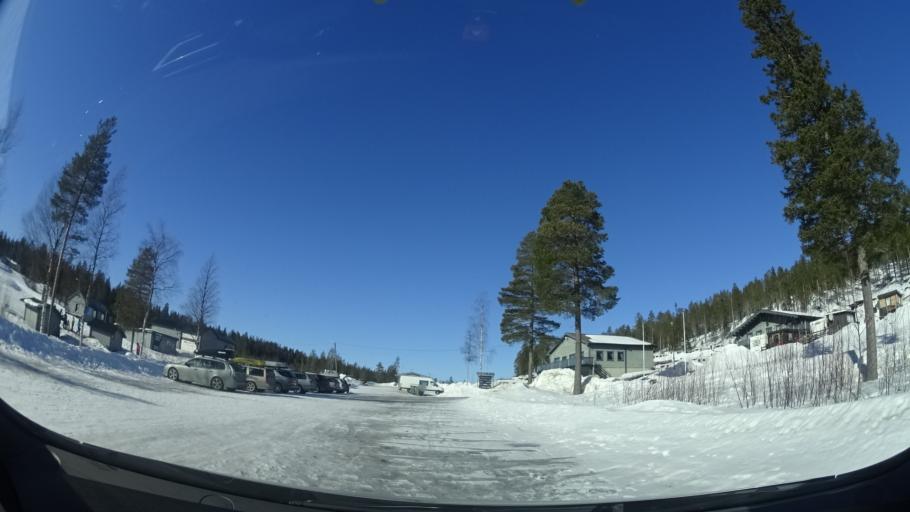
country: SE
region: Vaesterbotten
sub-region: Skelleftea Kommun
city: Langsele
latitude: 65.1632
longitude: 20.1344
